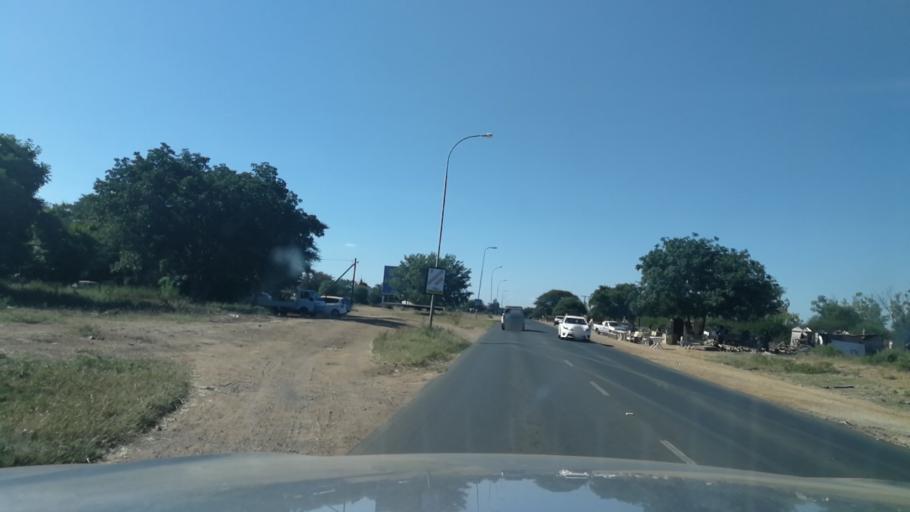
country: BW
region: South East
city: Gaborone
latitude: -24.6946
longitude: 25.8953
